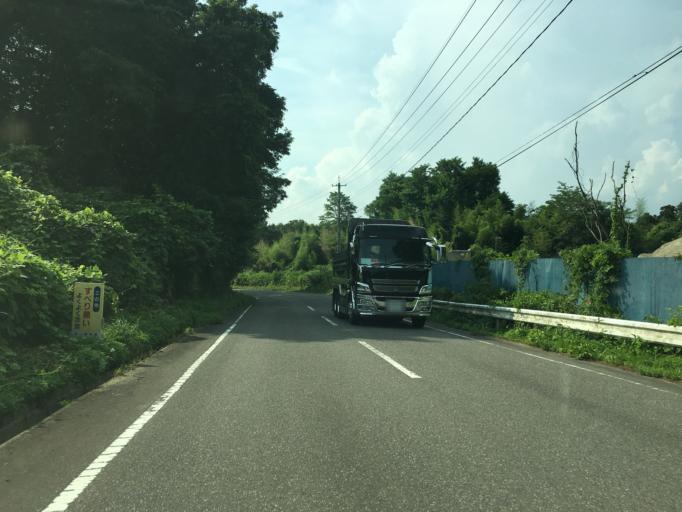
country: JP
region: Fukushima
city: Sukagawa
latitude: 37.3310
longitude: 140.4279
